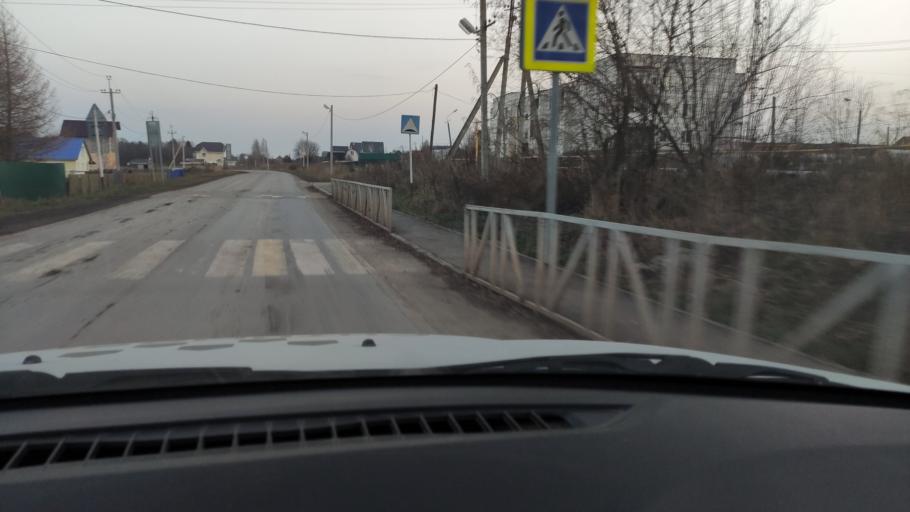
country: RU
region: Perm
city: Bershet'
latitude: 57.8040
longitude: 56.3675
